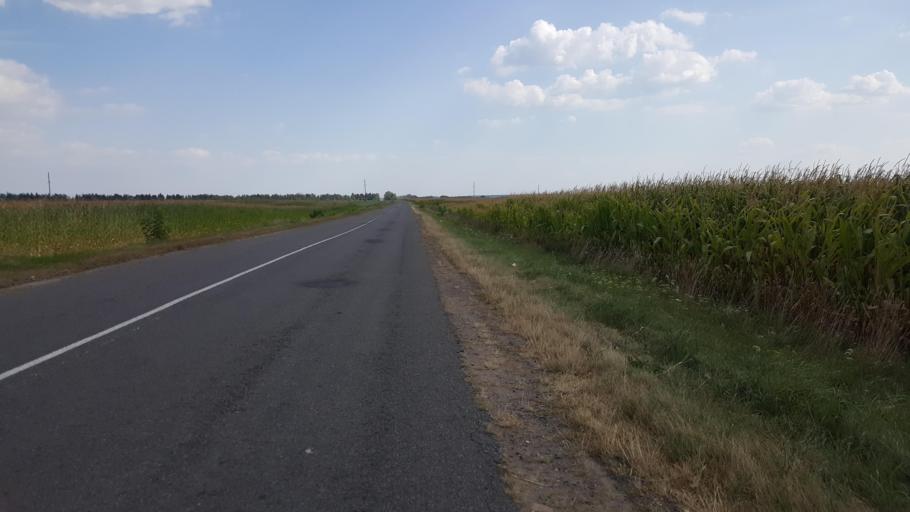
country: BY
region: Brest
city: Kamyanyets
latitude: 52.4240
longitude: 23.7715
